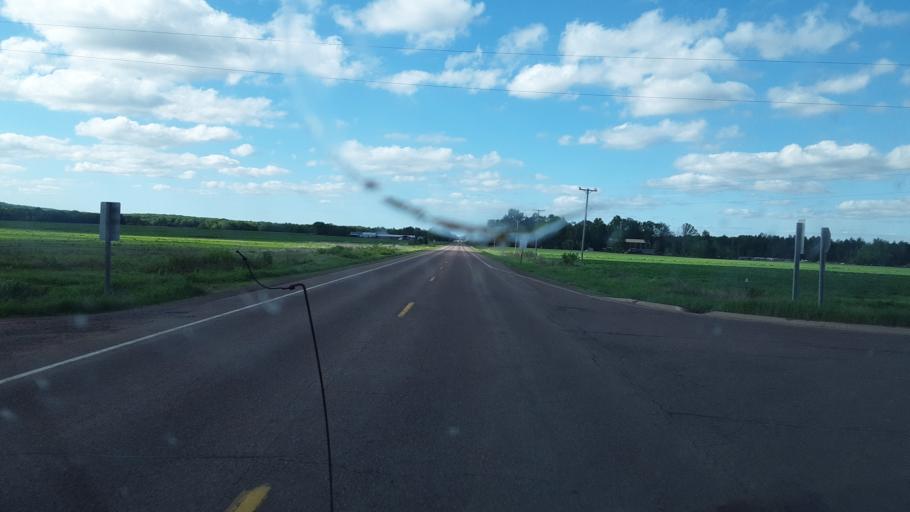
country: US
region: Wisconsin
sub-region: Wood County
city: Marshfield
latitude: 44.4821
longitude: -90.1809
